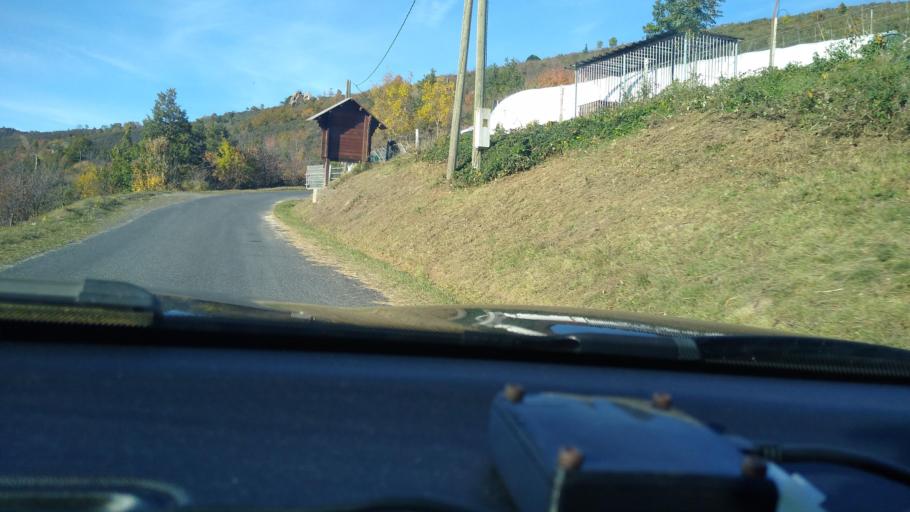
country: FR
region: Languedoc-Roussillon
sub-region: Departement de l'Aude
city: Quillan
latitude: 42.7209
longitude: 2.1233
